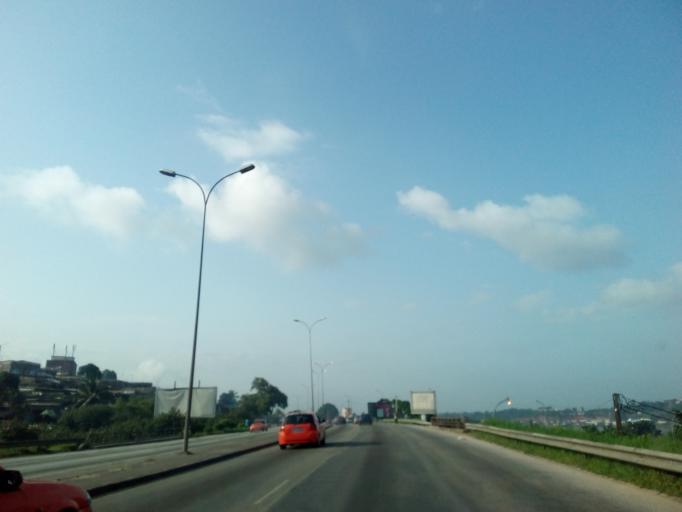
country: CI
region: Lagunes
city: Abidjan
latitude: 5.3480
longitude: -4.0396
